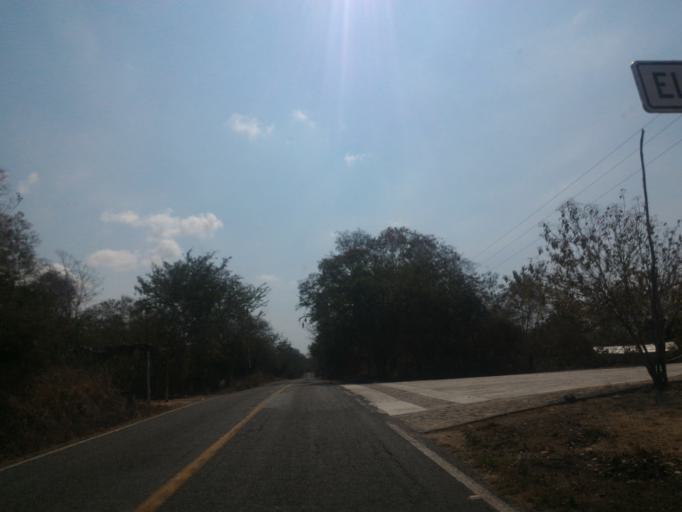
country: MX
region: Michoacan
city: Coahuayana Viejo
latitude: 18.3857
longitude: -103.5227
